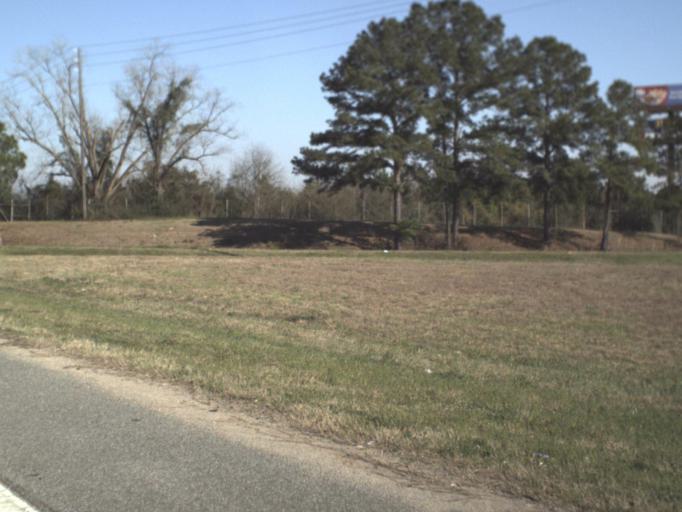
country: US
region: Florida
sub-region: Jackson County
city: Marianna
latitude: 30.7536
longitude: -85.2716
